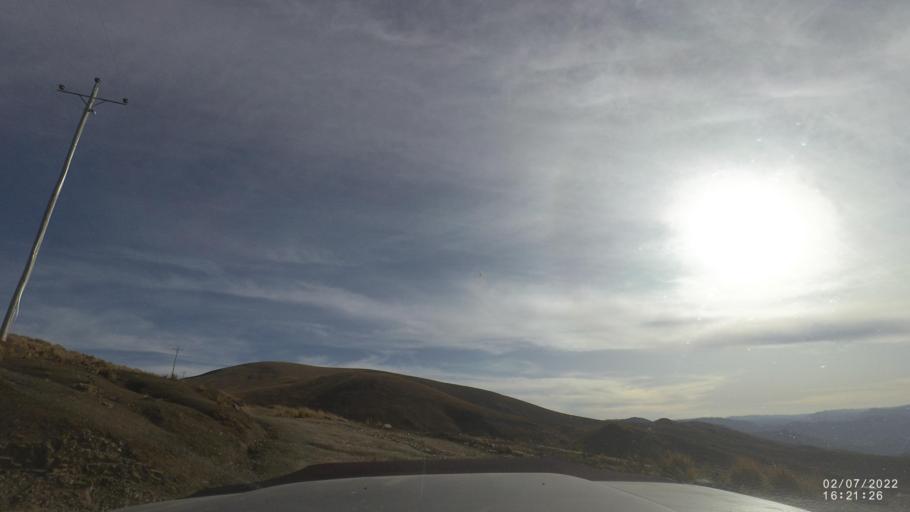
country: BO
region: Cochabamba
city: Irpa Irpa
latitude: -17.9314
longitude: -66.4518
